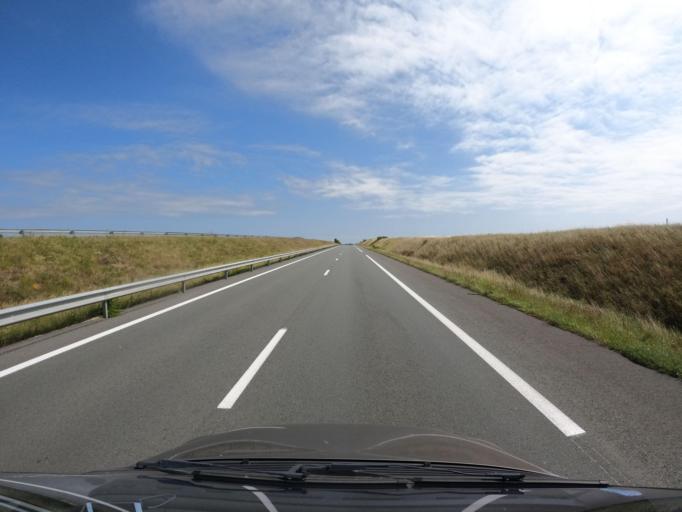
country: FR
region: Poitou-Charentes
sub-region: Departement des Deux-Sevres
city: Mauze-sur-le-Mignon
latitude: 46.2166
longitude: -0.6155
